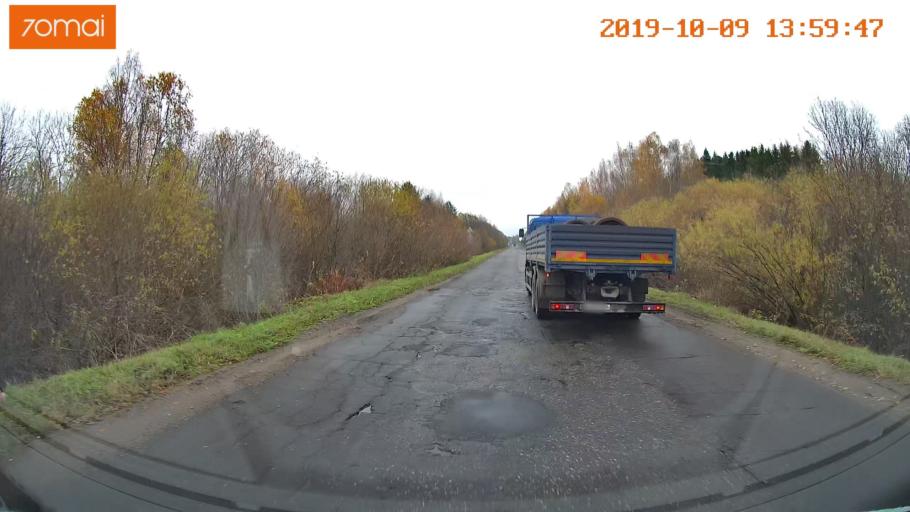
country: RU
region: Kostroma
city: Buy
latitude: 58.4367
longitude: 41.3273
